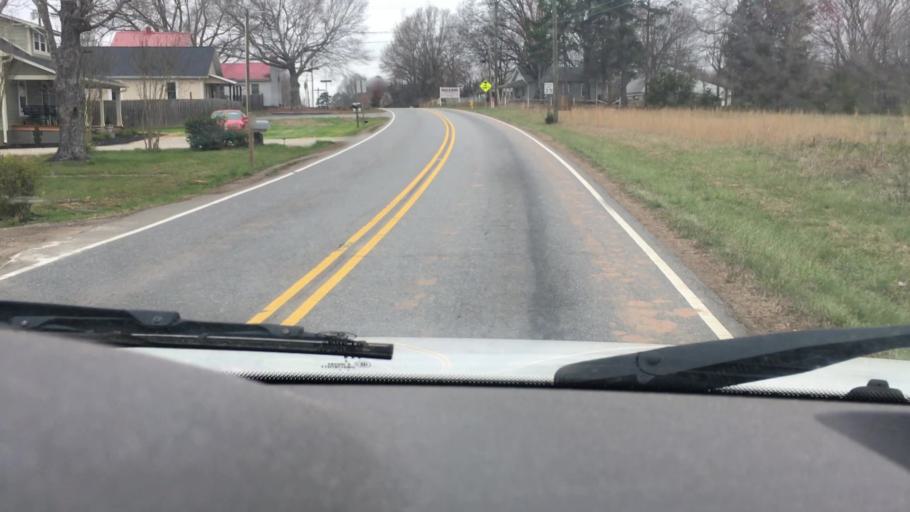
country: US
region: North Carolina
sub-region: Iredell County
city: Troutman
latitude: 35.6950
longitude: -80.8748
